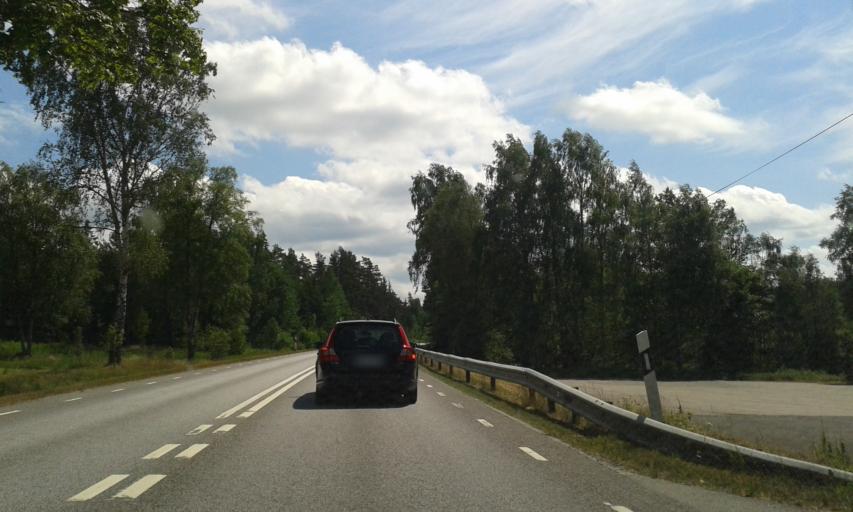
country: SE
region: Joenkoeping
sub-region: Varnamo Kommun
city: Rydaholm
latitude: 56.9698
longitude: 14.3317
